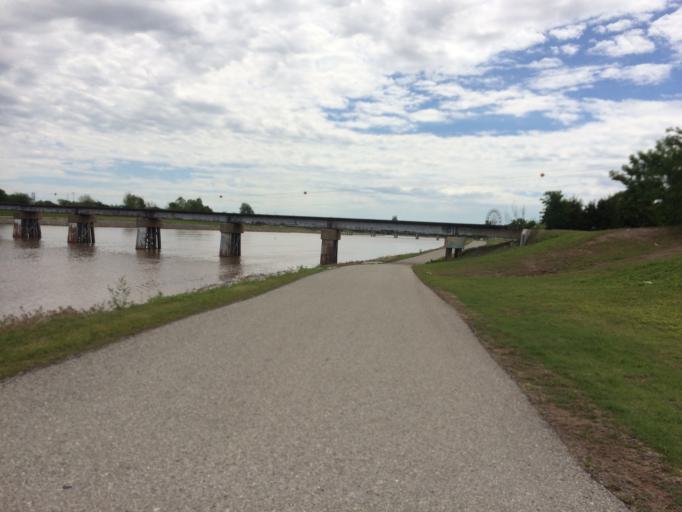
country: US
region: Oklahoma
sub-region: Oklahoma County
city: Oklahoma City
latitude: 35.4563
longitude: -97.5361
